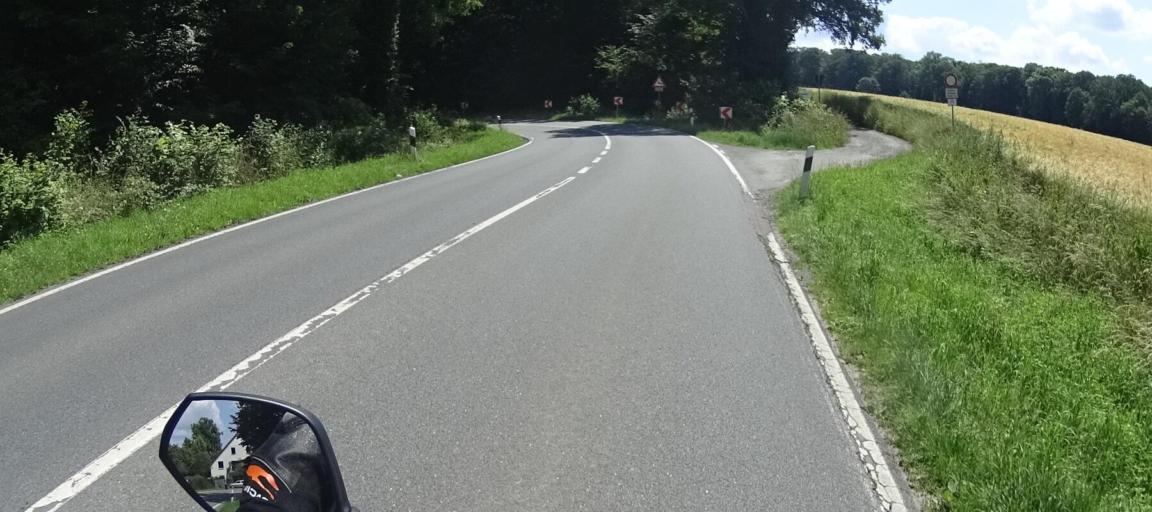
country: DE
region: North Rhine-Westphalia
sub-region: Regierungsbezirk Detmold
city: Hoexter
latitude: 51.7702
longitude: 9.4155
